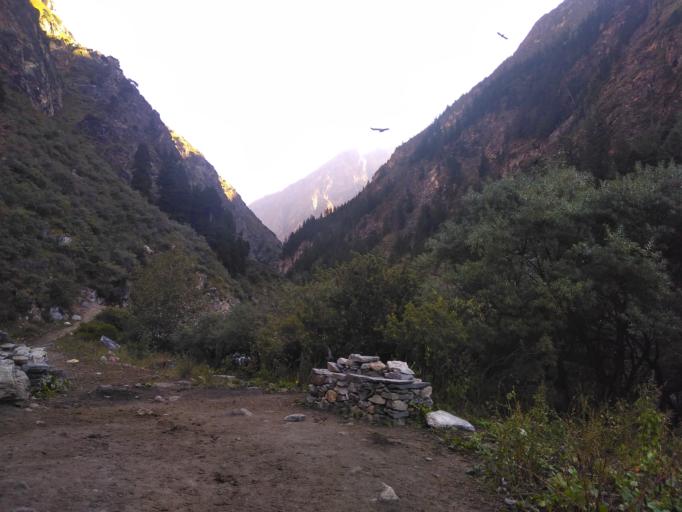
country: NP
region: Western Region
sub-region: Dhawalagiri Zone
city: Jomsom
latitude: 28.9255
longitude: 83.0375
